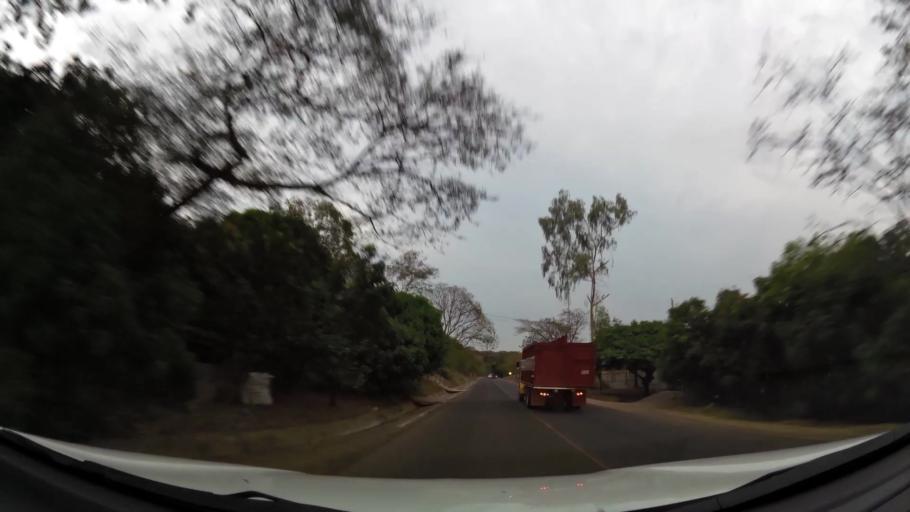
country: NI
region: Esteli
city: Esteli
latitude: 12.9955
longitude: -86.2954
